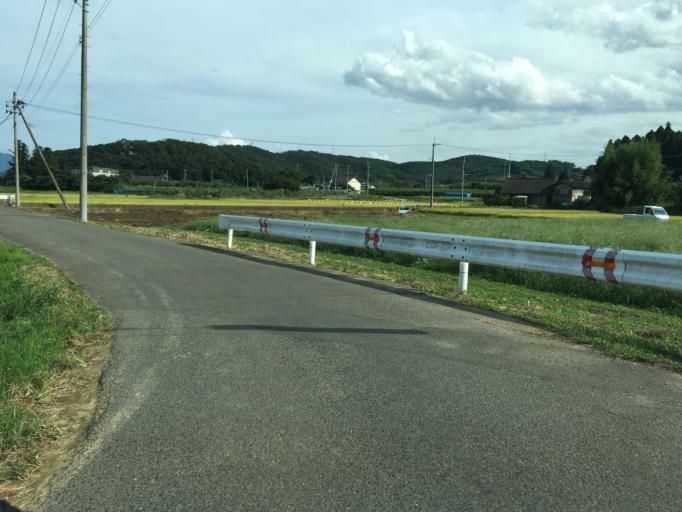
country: JP
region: Fukushima
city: Hobaramachi
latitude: 37.8144
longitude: 140.5256
